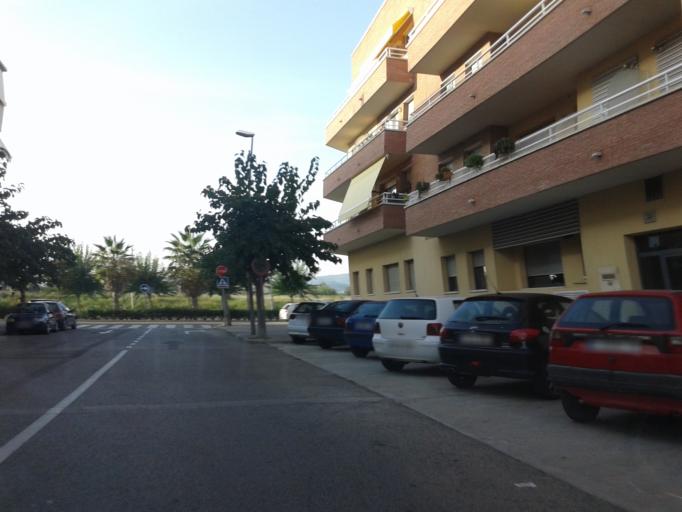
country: ES
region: Catalonia
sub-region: Provincia de Barcelona
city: Vilanova i la Geltru
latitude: 41.2286
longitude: 1.7208
